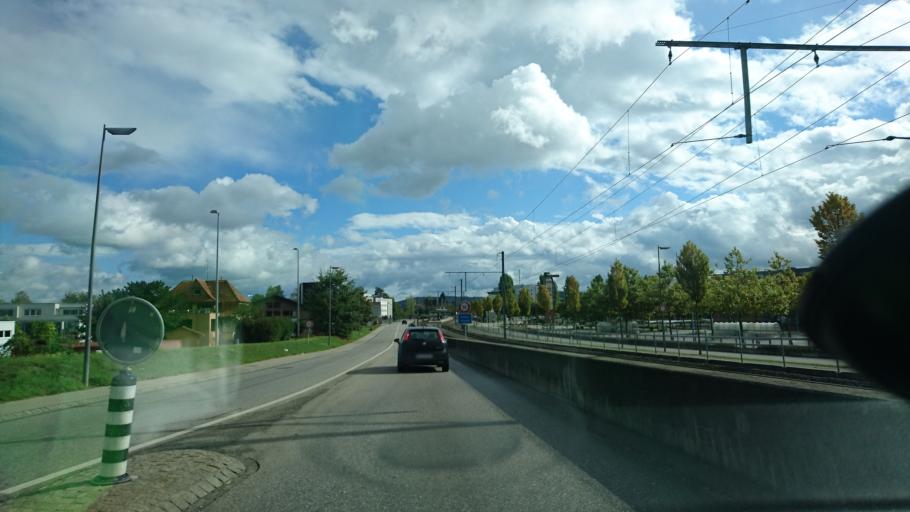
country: CH
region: Bern
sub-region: Bern-Mittelland District
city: Urtenen
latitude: 47.0182
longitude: 7.4902
